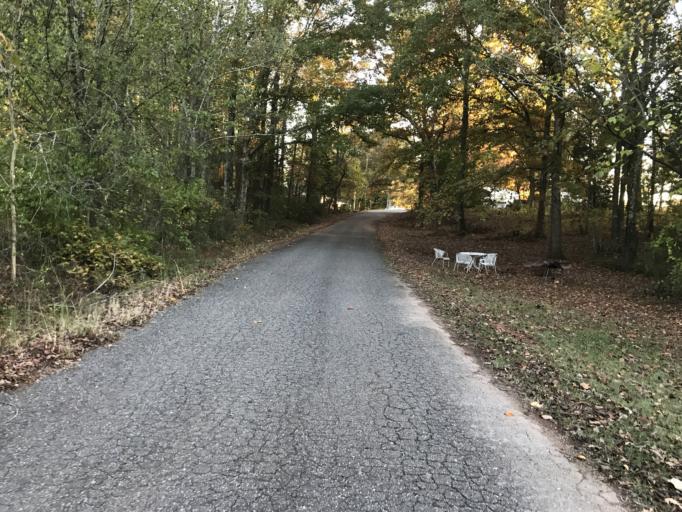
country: US
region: South Carolina
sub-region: Spartanburg County
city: Mayo
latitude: 35.1031
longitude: -81.7735
